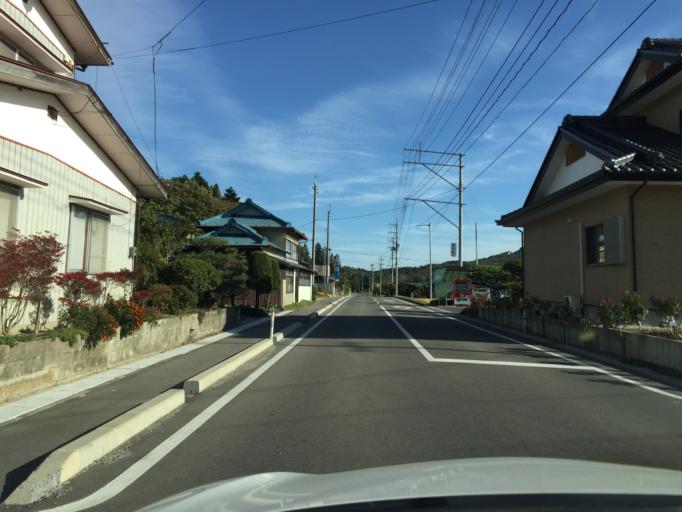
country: JP
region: Fukushima
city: Funehikimachi-funehiki
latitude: 37.3407
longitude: 140.5665
